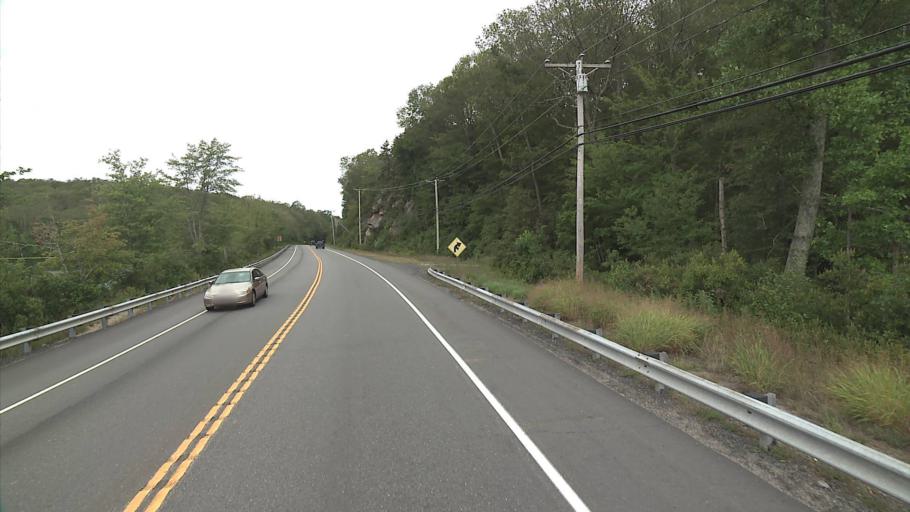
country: US
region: Connecticut
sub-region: New London County
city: Montville Center
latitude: 41.4622
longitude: -72.2489
